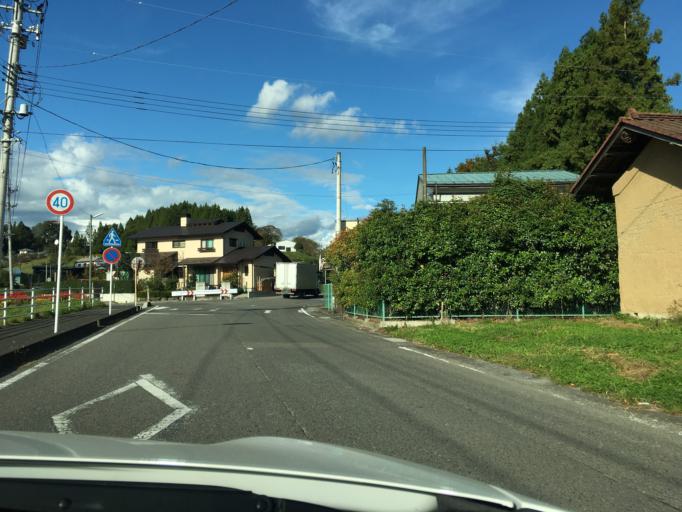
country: JP
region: Fukushima
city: Ishikawa
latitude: 37.2204
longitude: 140.4488
